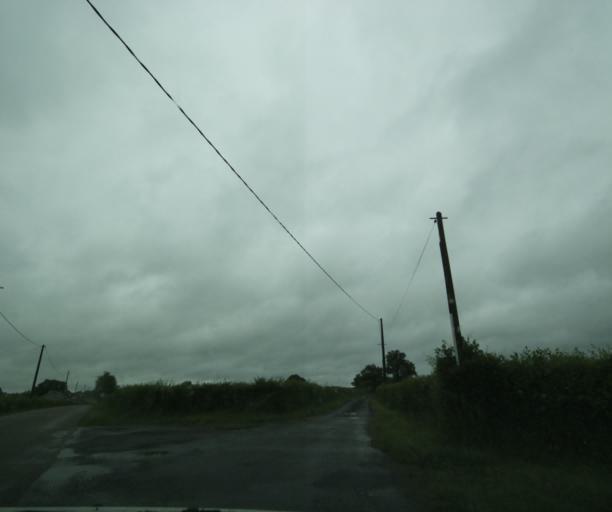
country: FR
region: Bourgogne
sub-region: Departement de Saone-et-Loire
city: Palinges
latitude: 46.5526
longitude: 4.1981
